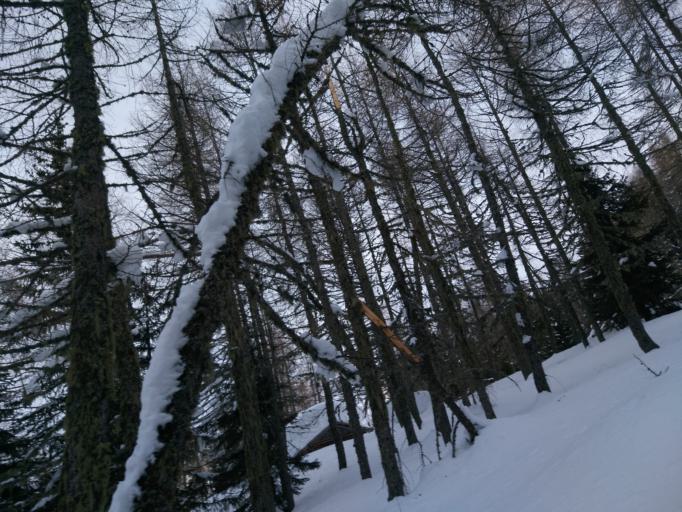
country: IT
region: Veneto
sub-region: Provincia di Belluno
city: Rocca Pietore
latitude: 46.4150
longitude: 11.9761
